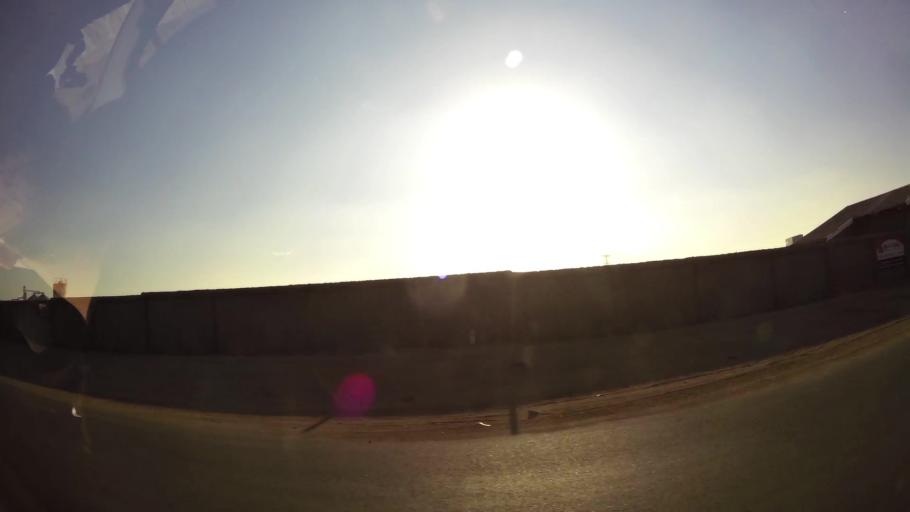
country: ZA
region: Gauteng
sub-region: West Rand District Municipality
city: Randfontein
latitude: -26.1943
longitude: 27.6913
